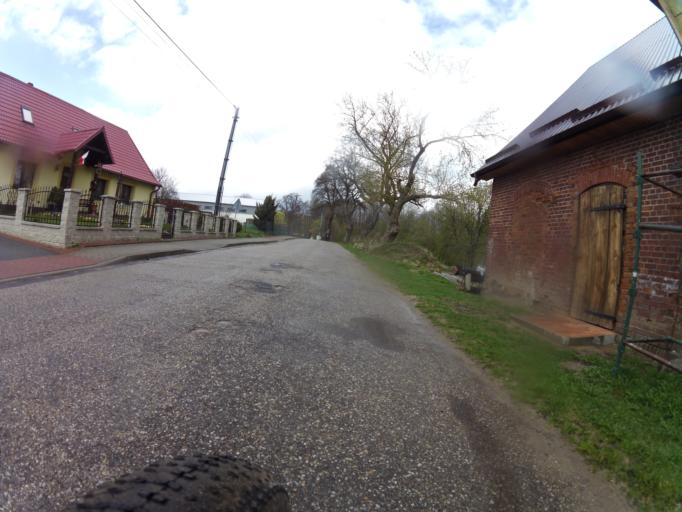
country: PL
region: Pomeranian Voivodeship
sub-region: Powiat slupski
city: Kepice
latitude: 54.2168
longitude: 16.7672
